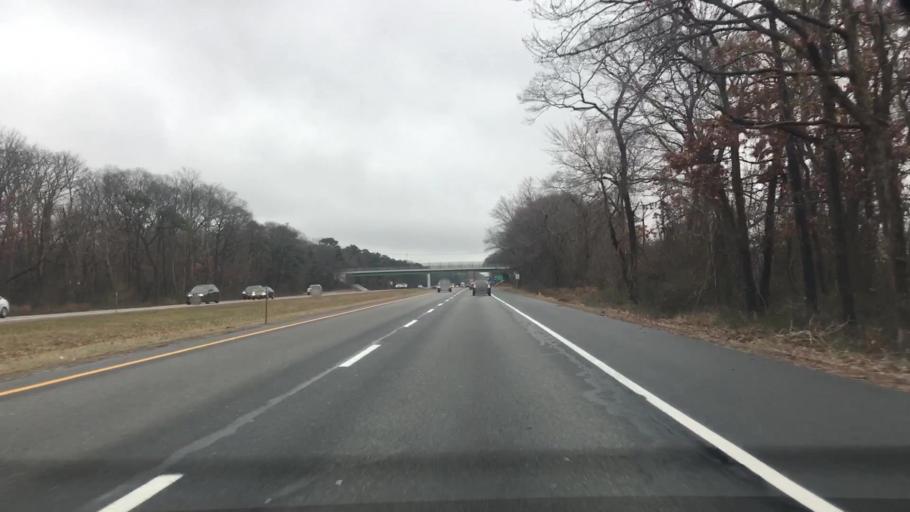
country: US
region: New York
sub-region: Suffolk County
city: Holtsville
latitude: 40.8284
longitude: -73.0557
